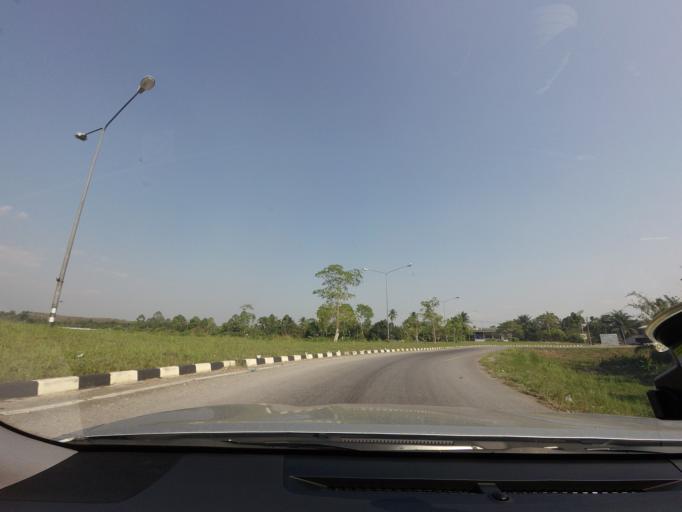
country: TH
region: Krabi
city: Plai Phraya
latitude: 8.6207
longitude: 99.0003
